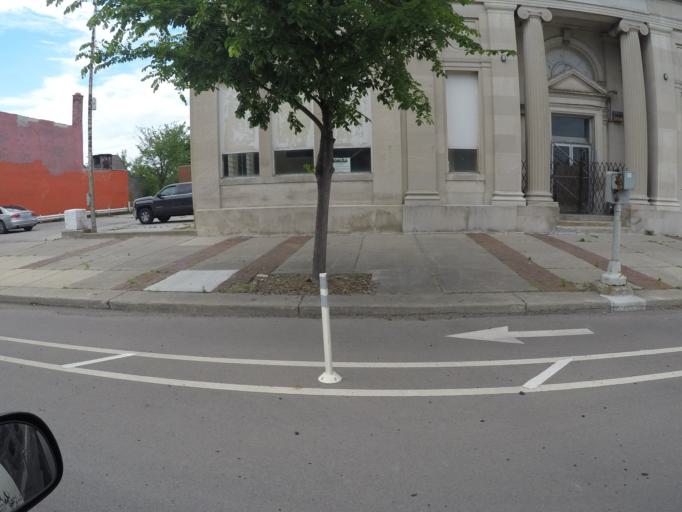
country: US
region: Michigan
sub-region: Wayne County
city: Grosse Pointe Park
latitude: 42.3738
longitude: -82.9424
